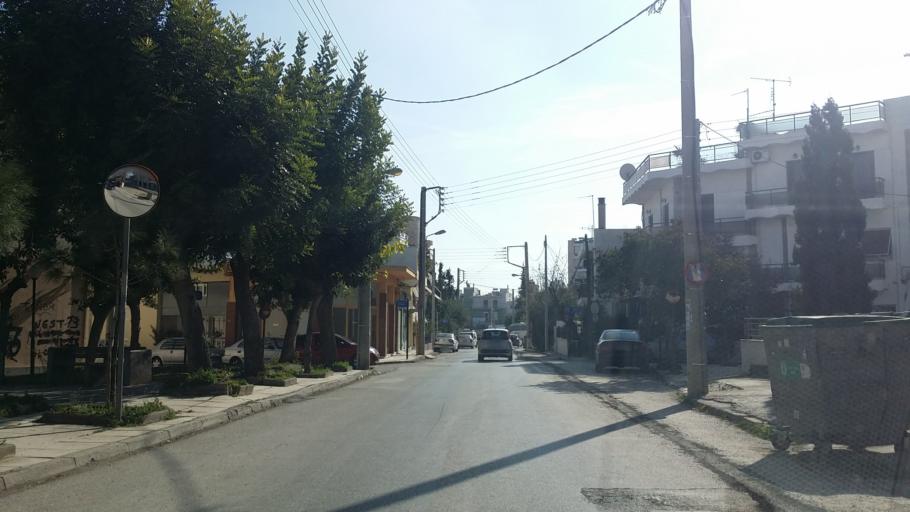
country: GR
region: Attica
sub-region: Nomarchia Athinas
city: Peristeri
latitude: 38.0193
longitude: 23.7067
